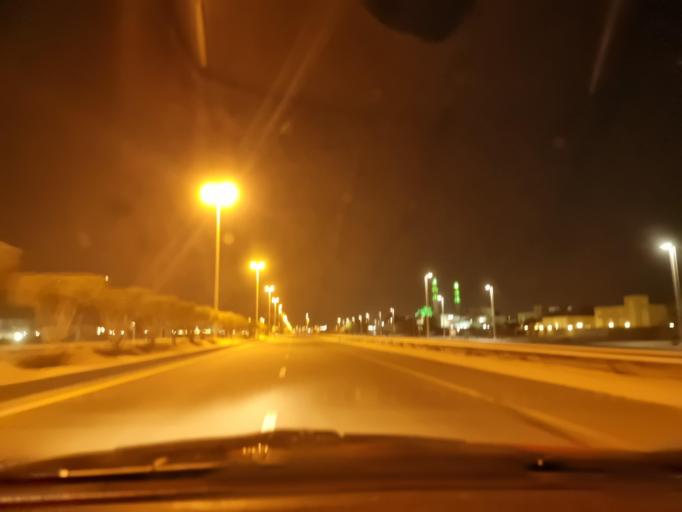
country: AE
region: Abu Dhabi
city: Abu Dhabi
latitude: 24.3718
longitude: 54.7013
